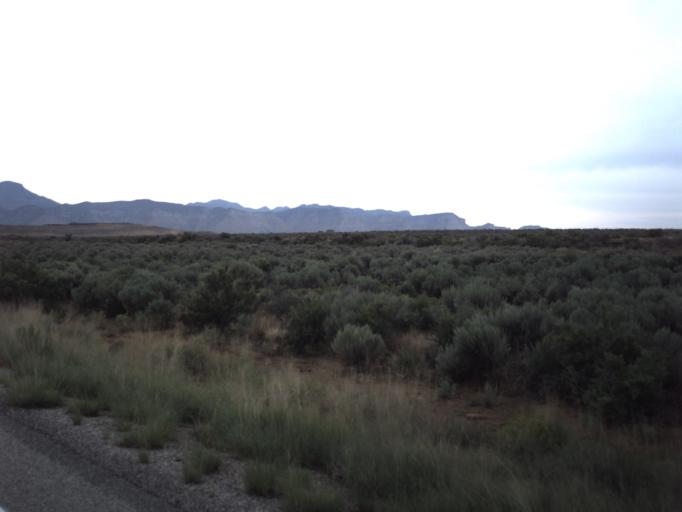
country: US
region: Utah
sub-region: Carbon County
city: East Carbon City
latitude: 39.5358
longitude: -110.5039
